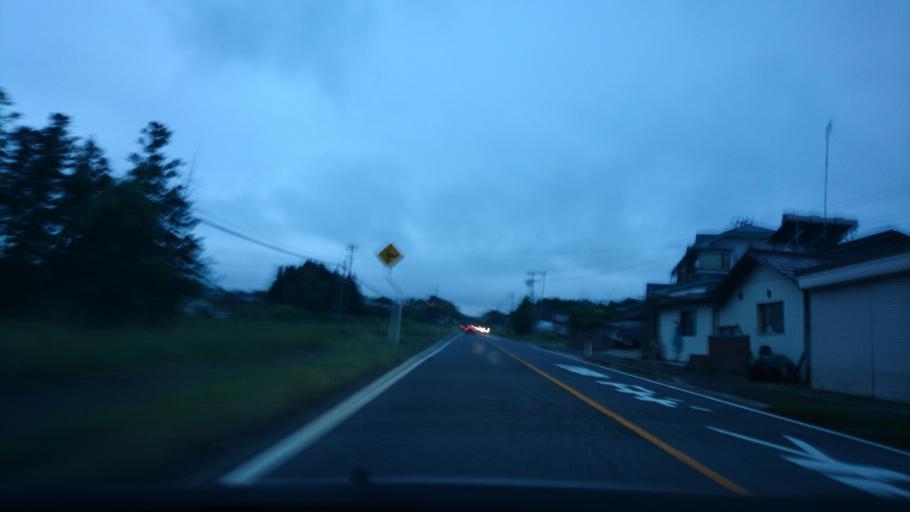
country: JP
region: Iwate
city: Ichinoseki
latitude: 38.8484
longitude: 141.0955
